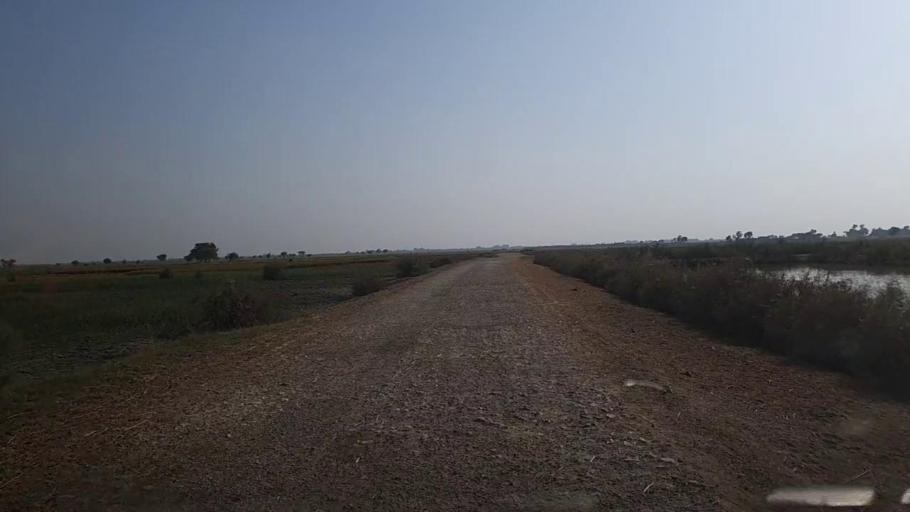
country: PK
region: Sindh
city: Kandhkot
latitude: 28.3780
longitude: 69.3343
